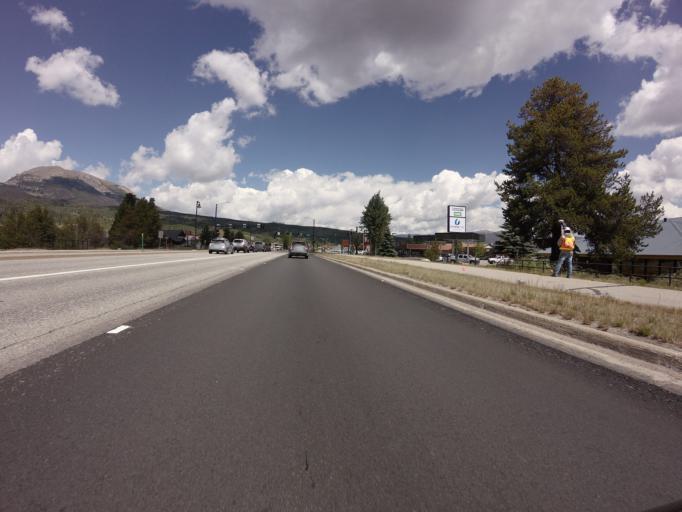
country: US
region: Colorado
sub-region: Summit County
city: Frisco
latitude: 39.5852
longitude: -106.0942
